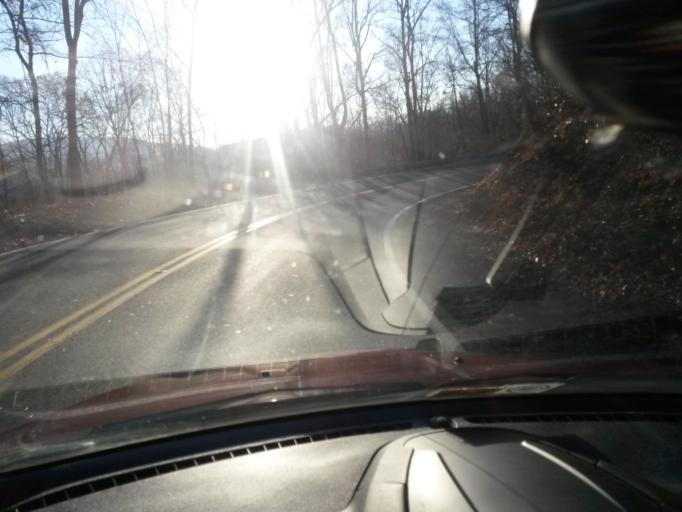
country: US
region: Virginia
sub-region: City of Buena Vista
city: Buena Vista
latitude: 37.7033
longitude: -79.2458
